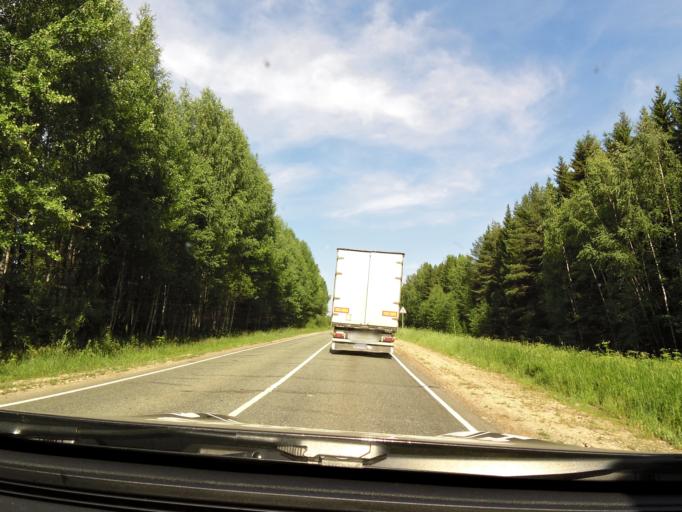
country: RU
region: Kirov
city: Belaya Kholunitsa
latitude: 58.8183
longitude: 50.6002
